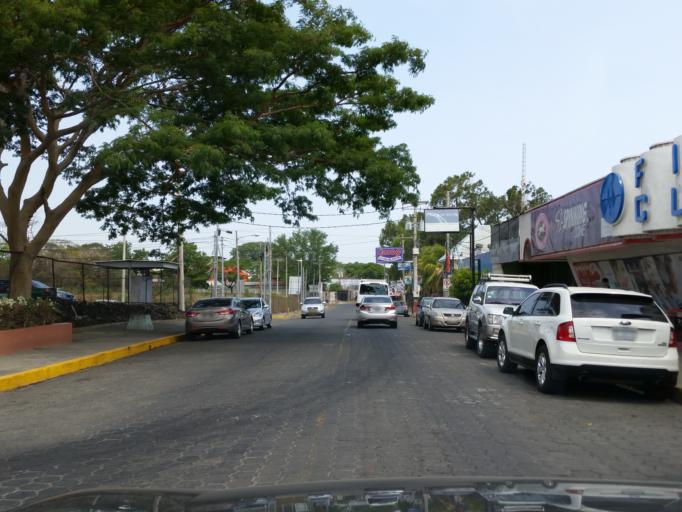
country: NI
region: Managua
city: Managua
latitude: 12.1107
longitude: -86.2553
